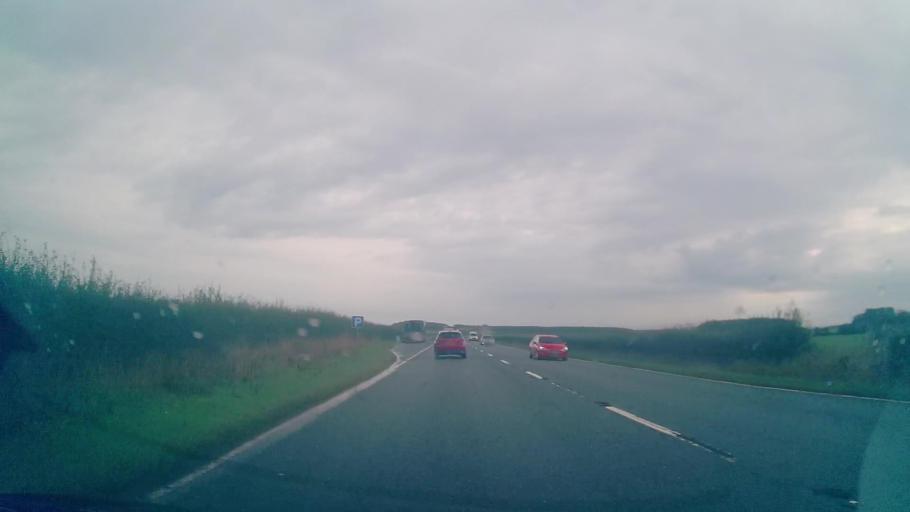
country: GB
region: Scotland
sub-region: Dumfries and Galloway
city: Annan
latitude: 55.0060
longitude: -3.3272
